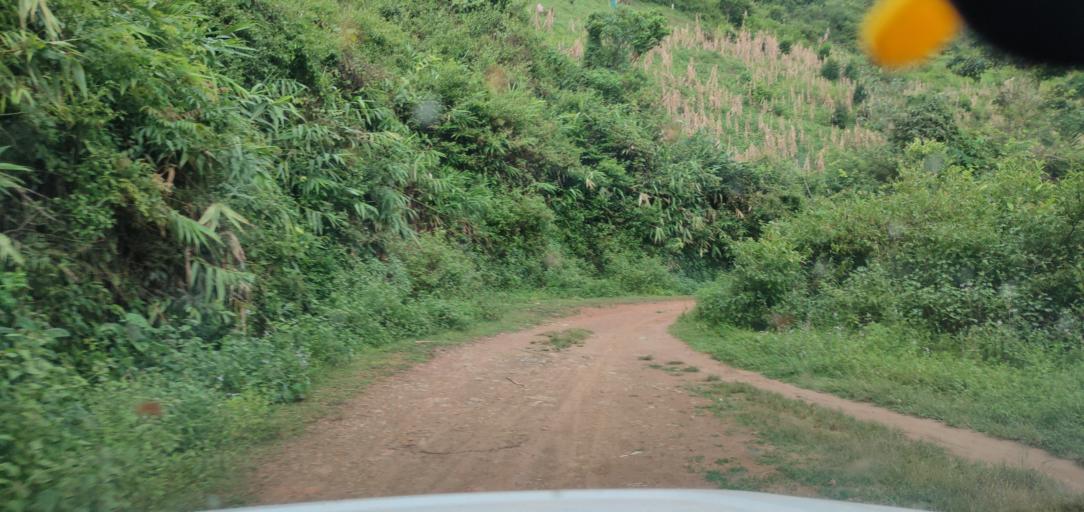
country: LA
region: Phongsali
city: Phongsali
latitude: 21.4471
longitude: 102.2912
